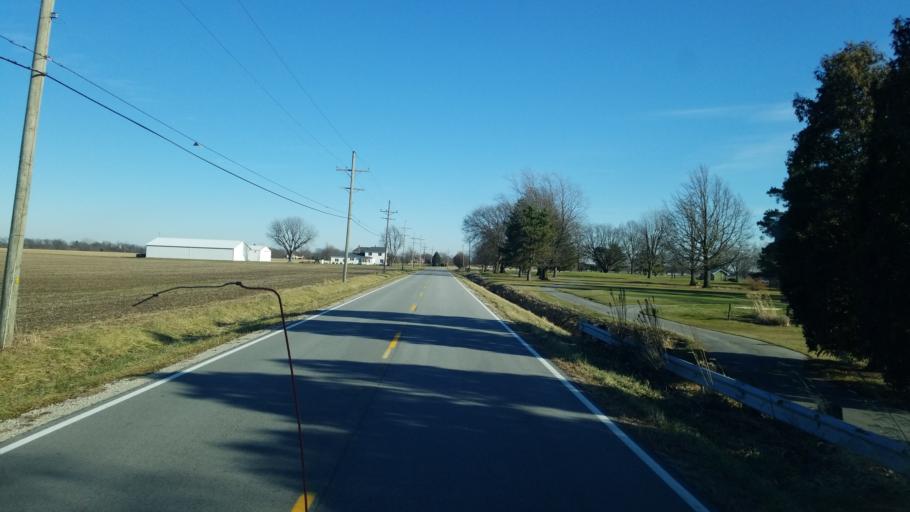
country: US
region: Ohio
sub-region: Sandusky County
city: Stony Prairie
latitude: 41.3494
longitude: -83.1912
